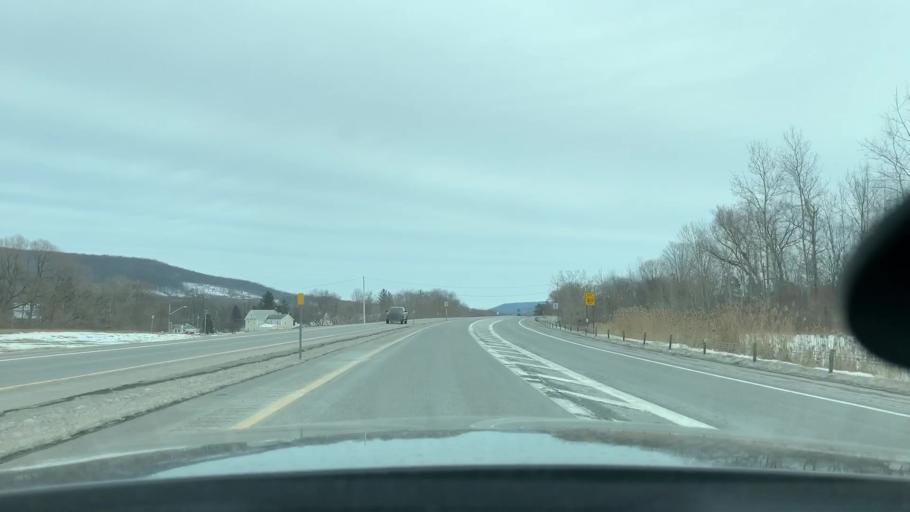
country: US
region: New York
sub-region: Herkimer County
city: Frankfort
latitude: 43.0245
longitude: -75.0598
